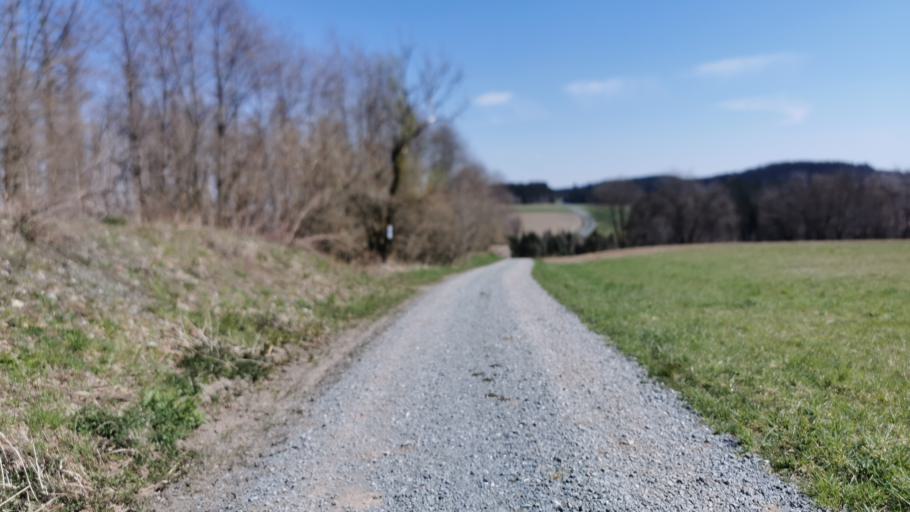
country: DE
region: Bavaria
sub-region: Upper Franconia
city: Pressig
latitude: 50.3702
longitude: 11.3423
